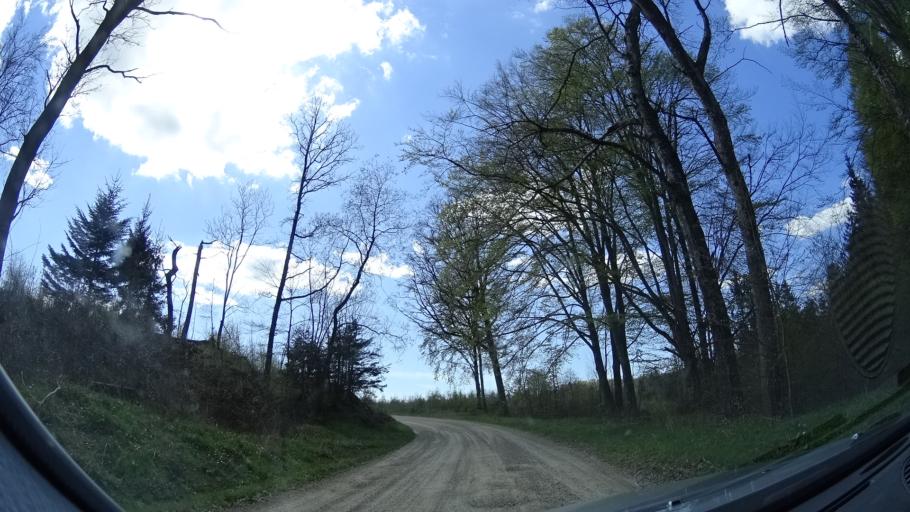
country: SE
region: Skane
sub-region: Hassleholms Kommun
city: Tormestorp
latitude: 56.0889
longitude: 13.7103
